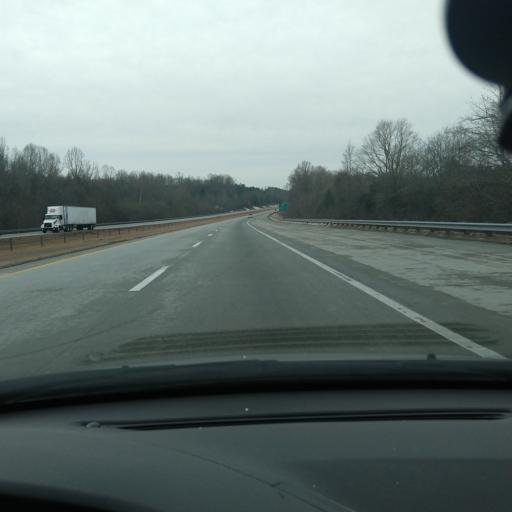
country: US
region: North Carolina
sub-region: Davidson County
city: Lexington
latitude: 35.8560
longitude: -80.2727
